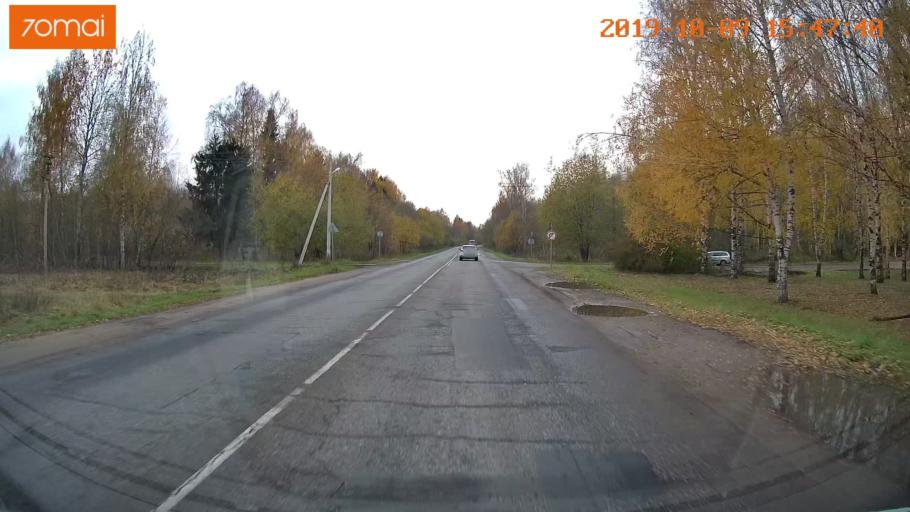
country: RU
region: Kostroma
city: Oktyabr'skiy
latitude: 57.8160
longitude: 41.0255
